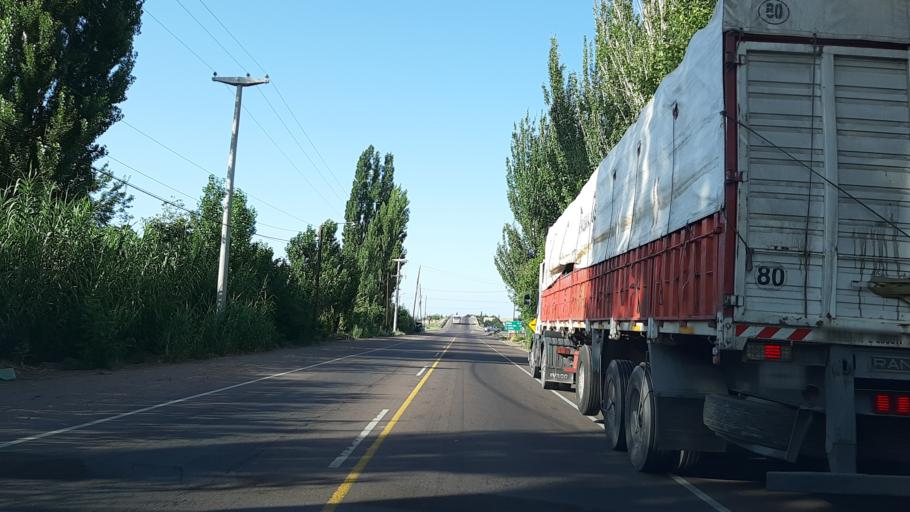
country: AR
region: Mendoza
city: San Martin
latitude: -33.0379
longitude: -68.5175
